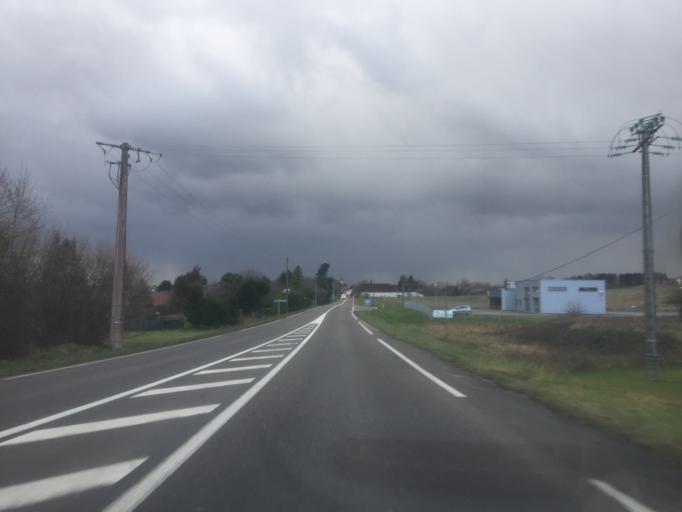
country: FR
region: Franche-Comte
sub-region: Departement du Jura
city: Dampierre
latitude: 47.1587
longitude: 5.7522
